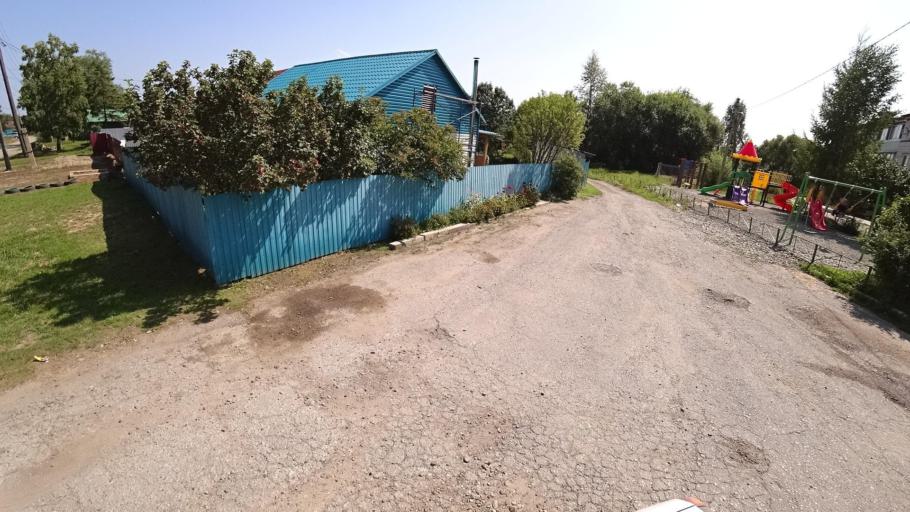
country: RU
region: Khabarovsk Krai
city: Khor
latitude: 47.9678
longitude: 135.0551
